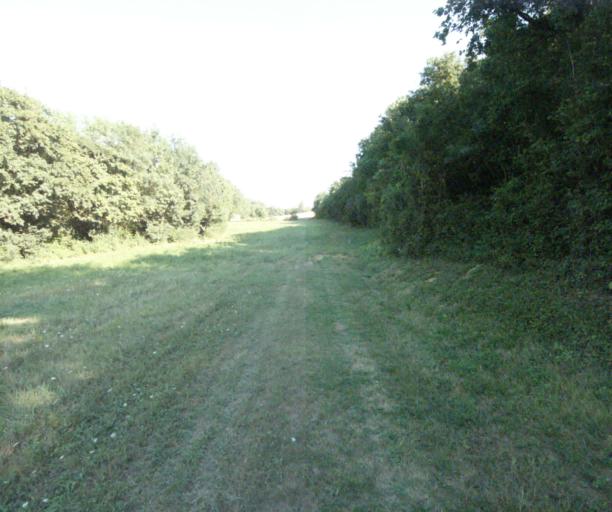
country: FR
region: Midi-Pyrenees
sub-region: Departement de la Haute-Garonne
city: Saint-Felix-Lauragais
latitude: 43.4341
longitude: 1.8238
